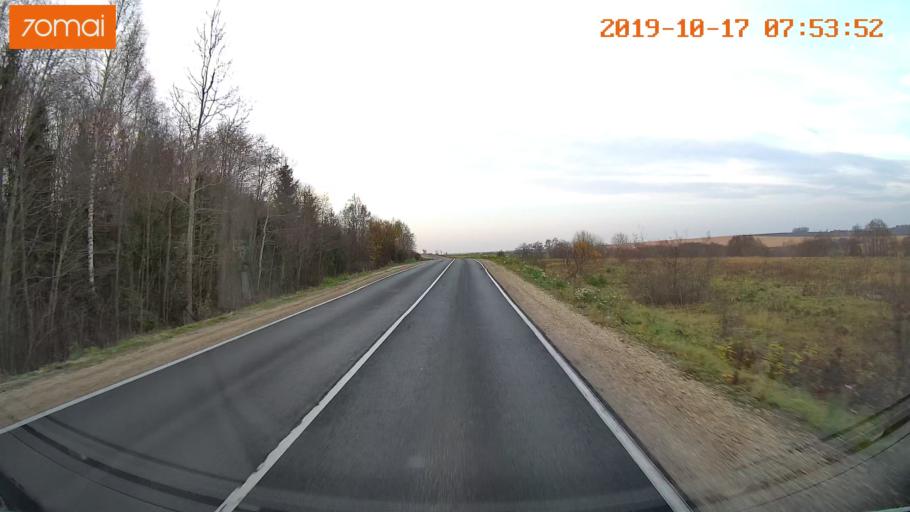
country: RU
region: Vladimir
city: Bavleny
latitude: 56.4567
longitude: 39.6136
